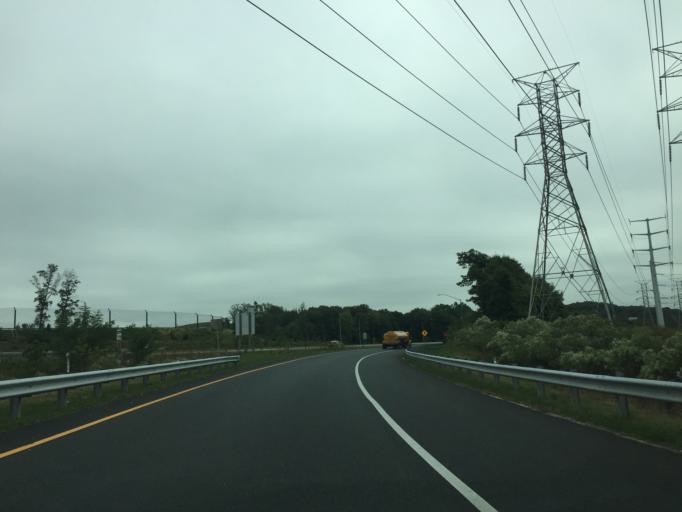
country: US
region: Maryland
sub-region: Baltimore County
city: White Marsh
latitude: 39.3780
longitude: -76.4459
